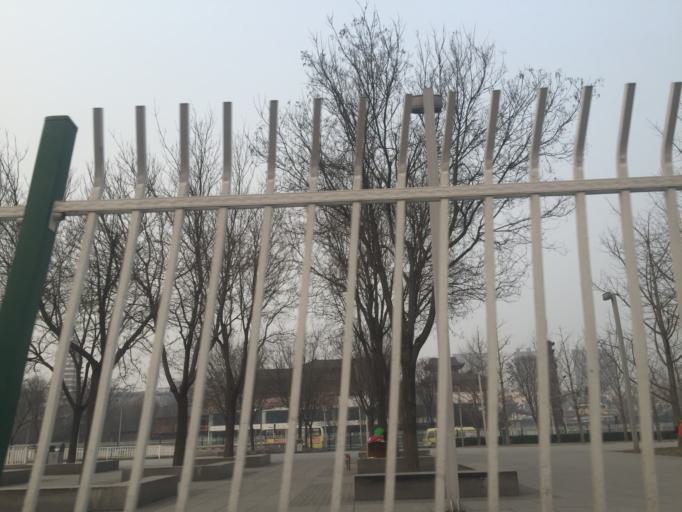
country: CN
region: Beijing
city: Datun
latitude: 39.9806
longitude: 116.3882
